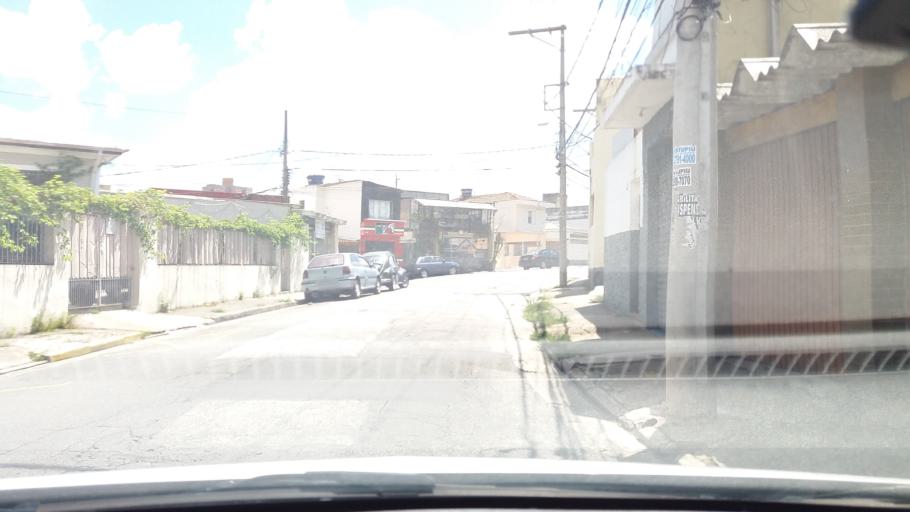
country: BR
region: Sao Paulo
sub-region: Sao Paulo
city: Sao Paulo
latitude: -23.4806
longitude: -46.6268
